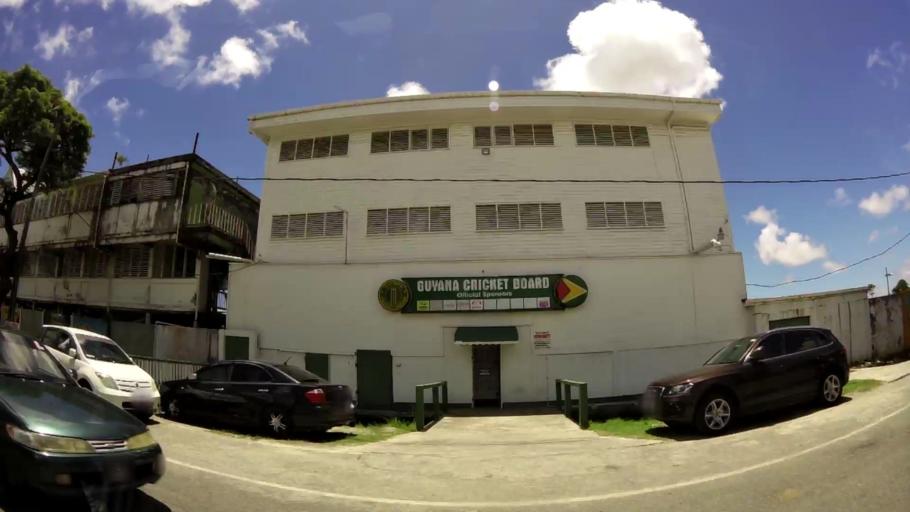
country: GY
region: Demerara-Mahaica
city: Georgetown
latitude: 6.8074
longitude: -58.1501
